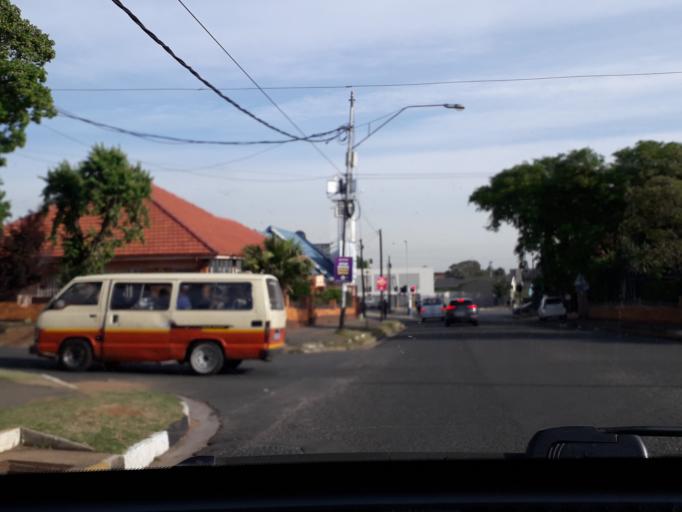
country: ZA
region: Gauteng
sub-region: City of Johannesburg Metropolitan Municipality
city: Johannesburg
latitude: -26.1401
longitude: 28.0884
